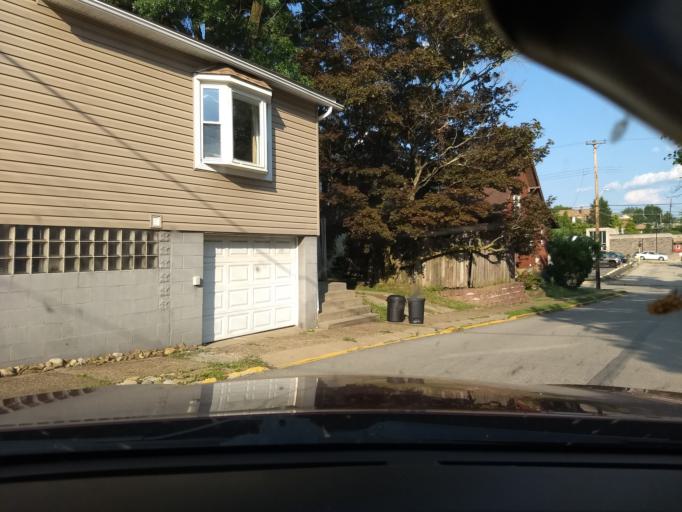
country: US
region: Pennsylvania
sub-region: Allegheny County
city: North Versailles
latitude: 40.3823
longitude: -79.8123
